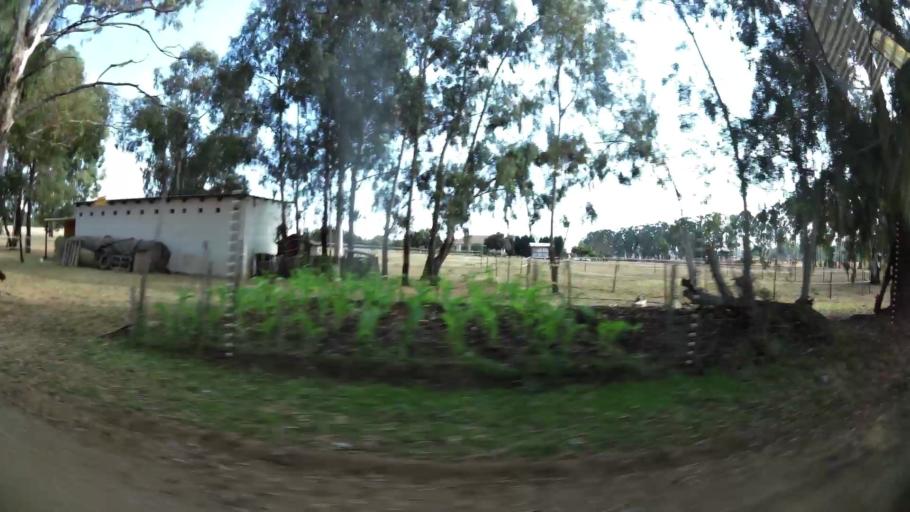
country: ZA
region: Gauteng
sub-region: Ekurhuleni Metropolitan Municipality
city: Benoni
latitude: -26.0870
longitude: 28.3667
